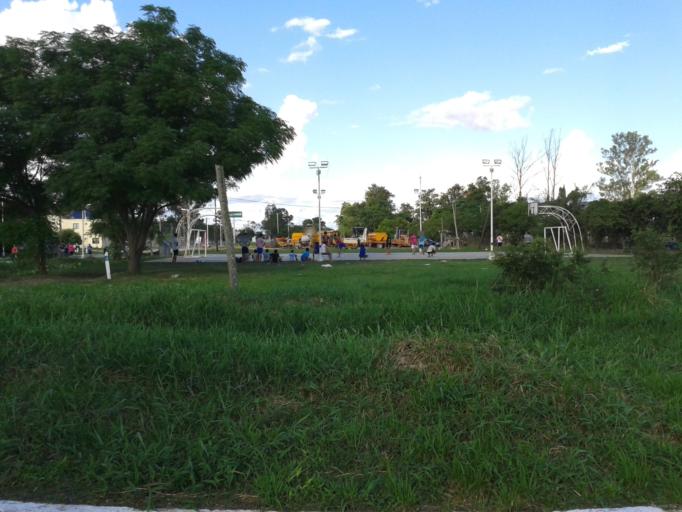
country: AR
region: Formosa
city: Clorinda
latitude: -25.2899
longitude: -57.7269
